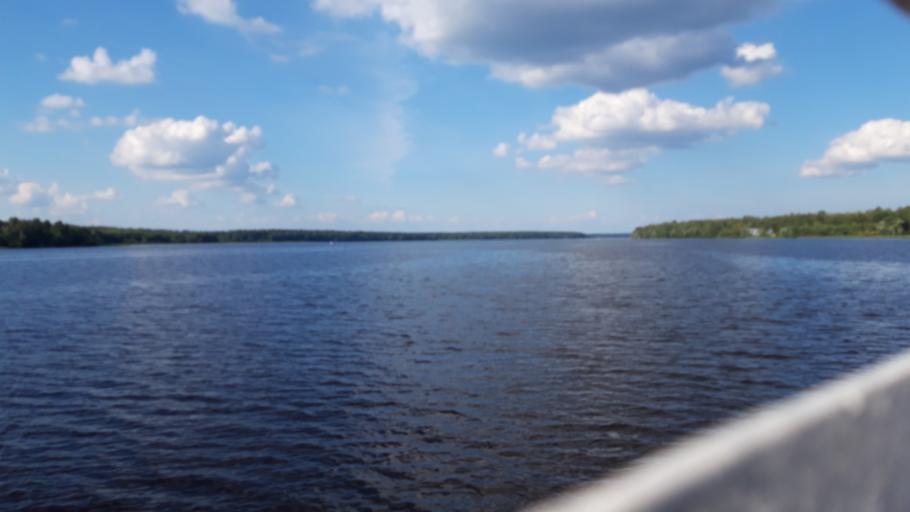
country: RU
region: Tverskaya
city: Konakovo
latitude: 56.6782
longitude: 36.6824
